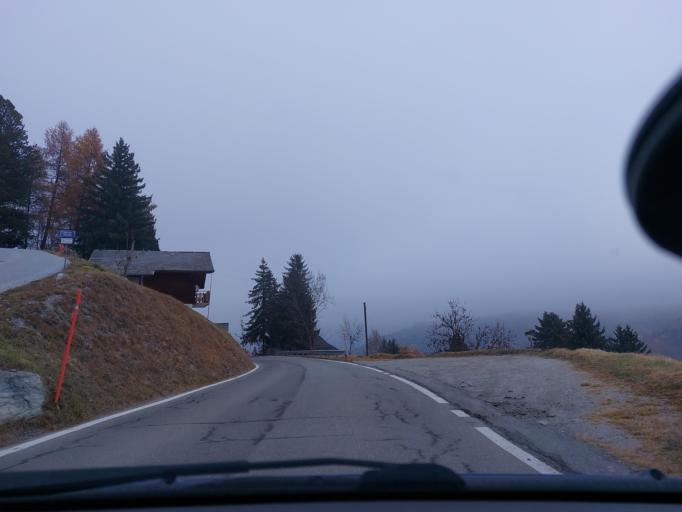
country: CH
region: Valais
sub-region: Conthey District
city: Basse-Nendaz
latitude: 46.1723
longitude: 7.3118
